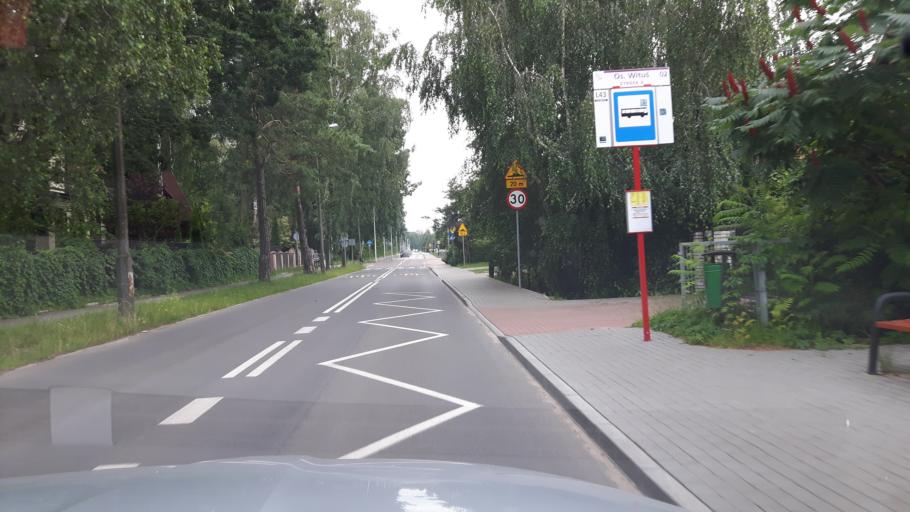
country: PL
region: Masovian Voivodeship
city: Zielonka
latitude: 52.2975
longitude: 21.1618
